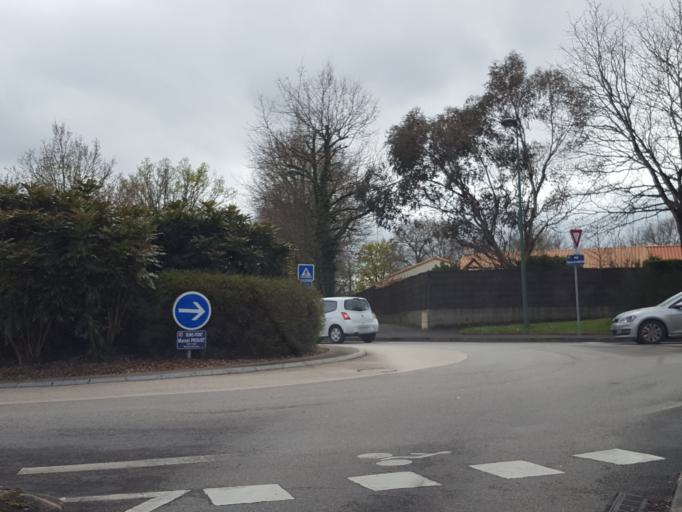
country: FR
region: Pays de la Loire
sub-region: Departement de la Vendee
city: La Roche-sur-Yon
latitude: 46.6683
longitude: -1.3981
